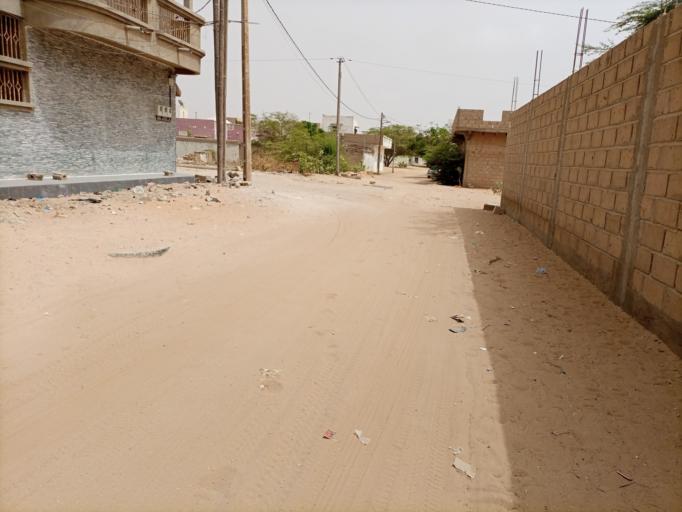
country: SN
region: Saint-Louis
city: Saint-Louis
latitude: 16.0398
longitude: -16.4418
